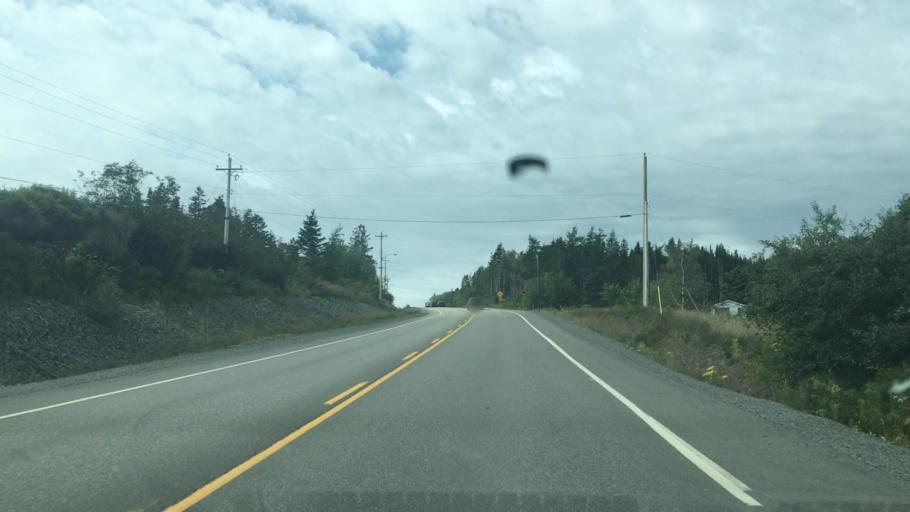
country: CA
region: Nova Scotia
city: Princeville
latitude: 45.6787
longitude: -60.7847
